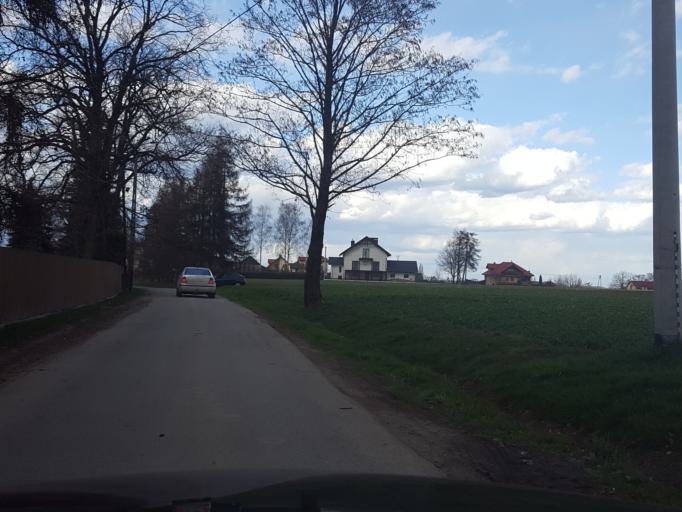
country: PL
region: Silesian Voivodeship
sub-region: Powiat bielski
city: Zabrzeg
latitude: 49.9547
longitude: 18.9083
